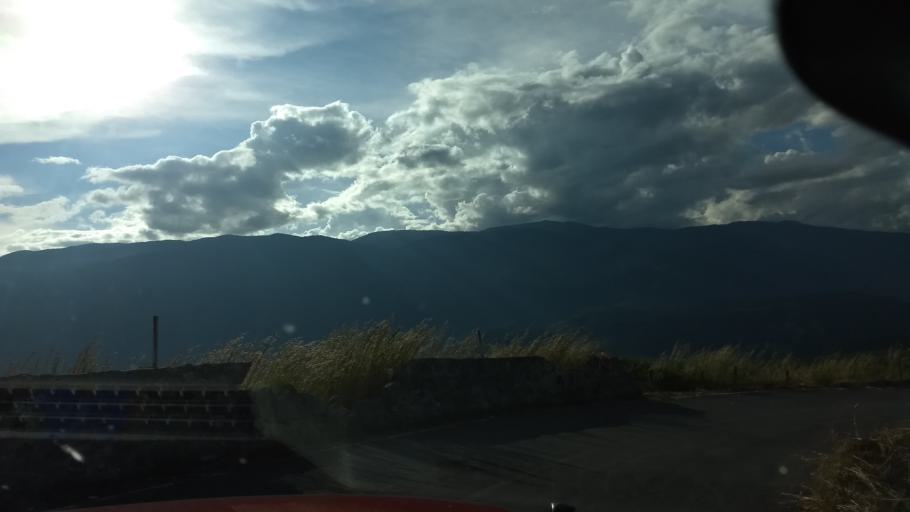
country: MX
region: Colima
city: Suchitlan
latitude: 19.4579
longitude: -103.7941
